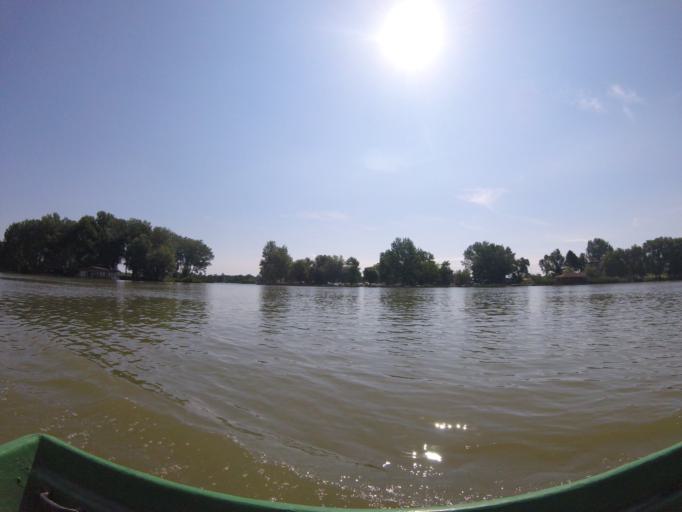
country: HU
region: Jasz-Nagykun-Szolnok
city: Tiszafured
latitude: 47.6085
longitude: 20.7165
